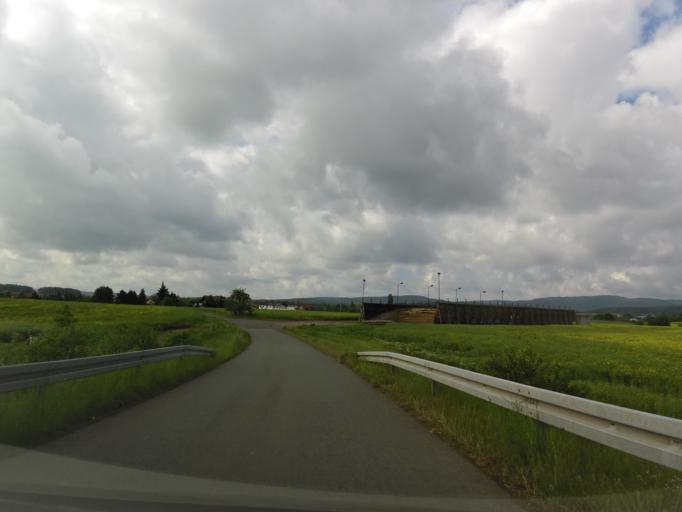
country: DE
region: Thuringia
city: Horselgau
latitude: 50.9063
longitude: 10.5984
